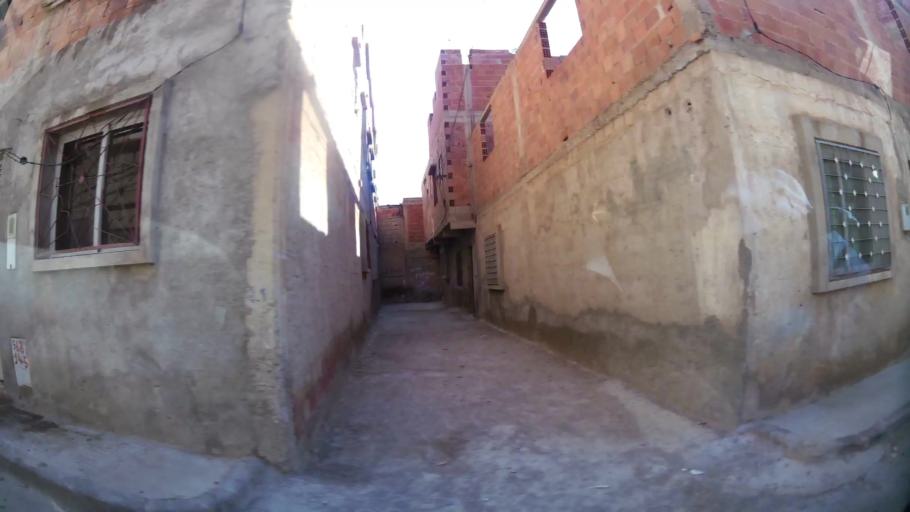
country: MA
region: Oriental
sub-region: Oujda-Angad
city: Oujda
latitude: 34.7202
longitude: -1.8832
